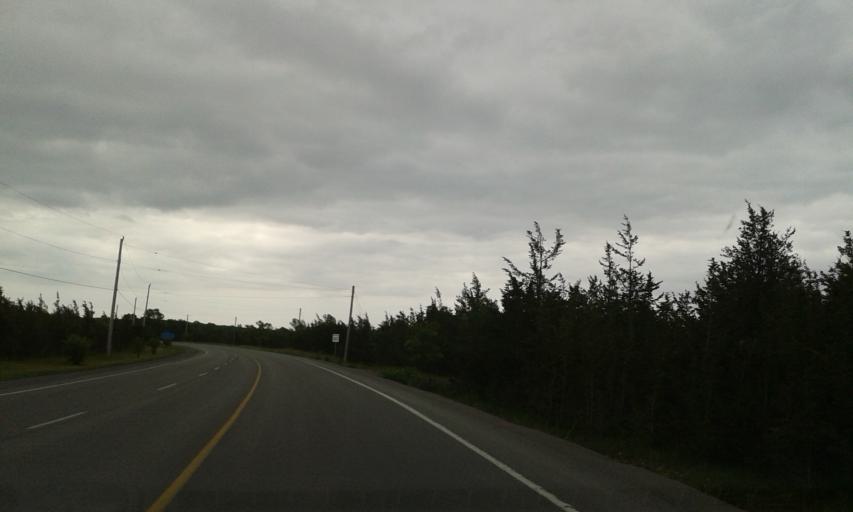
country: CA
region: Ontario
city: Quinte West
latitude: 43.9886
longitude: -77.5171
